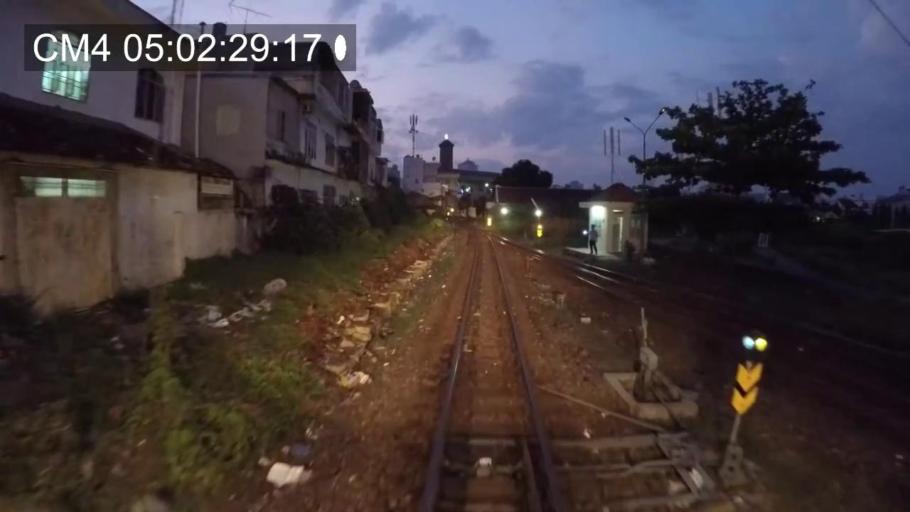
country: VN
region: Khanh Hoa
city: Nha Trang
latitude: 12.2510
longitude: 109.1754
